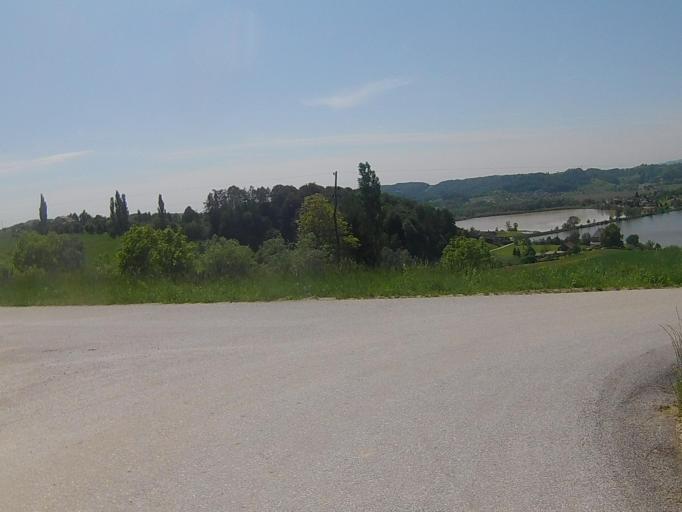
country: SI
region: Sveti Jurij v Slovenskih Goricah
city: Jurovski Dol
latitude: 46.5964
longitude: 15.7316
